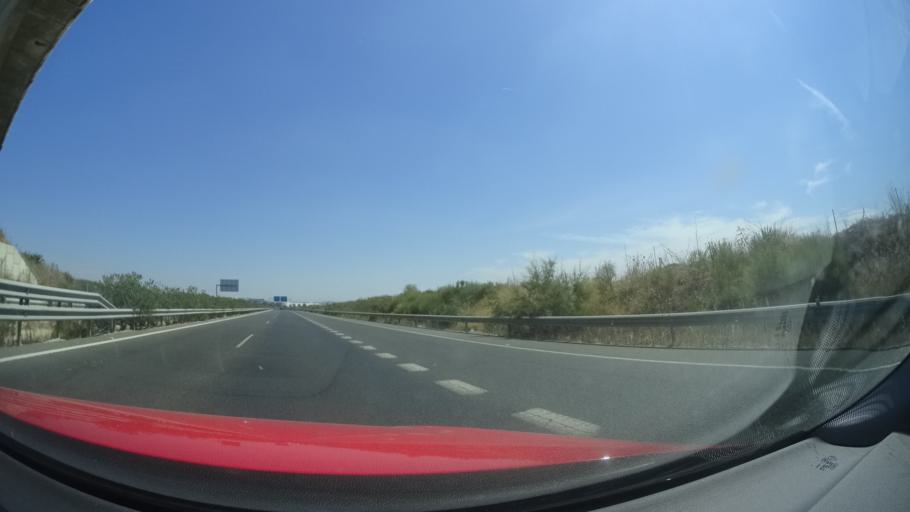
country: ES
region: Andalusia
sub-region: Provincia de Cadiz
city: Jerez de la Frontera
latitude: 36.7161
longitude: -6.1193
